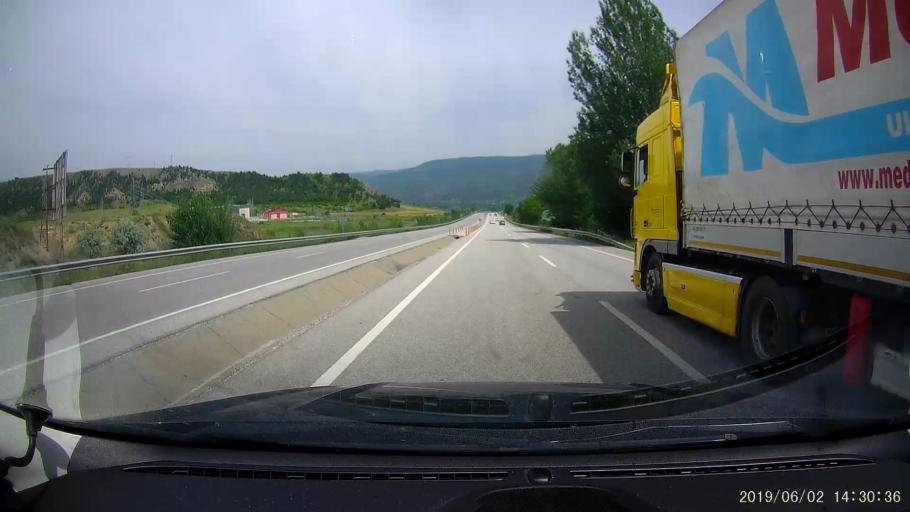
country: TR
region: Kastamonu
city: Tosya
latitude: 41.0167
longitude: 34.1189
